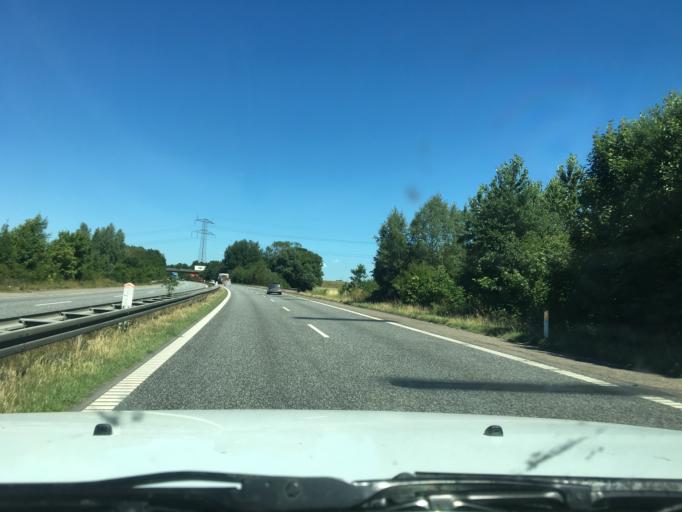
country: DK
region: Central Jutland
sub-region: Skanderborg Kommune
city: Horning
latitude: 56.1053
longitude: 10.0392
